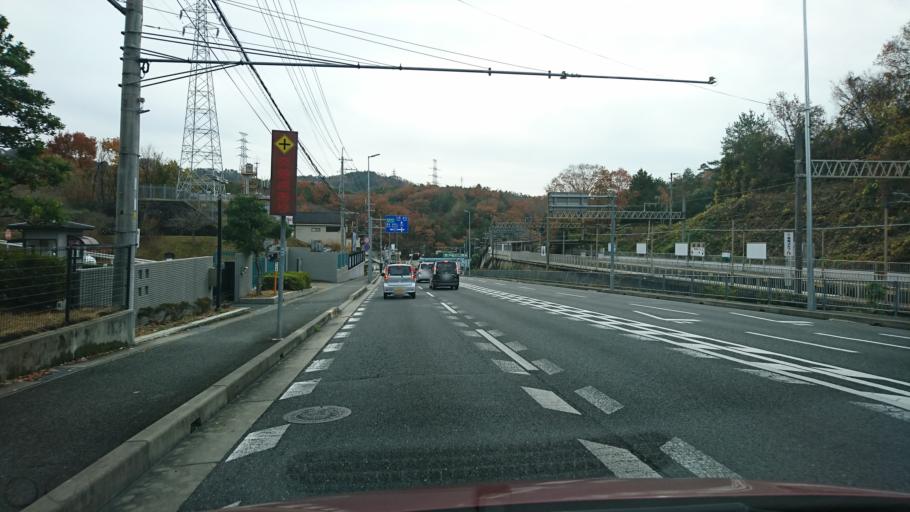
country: JP
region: Osaka
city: Ikeda
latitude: 34.8802
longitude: 135.4199
